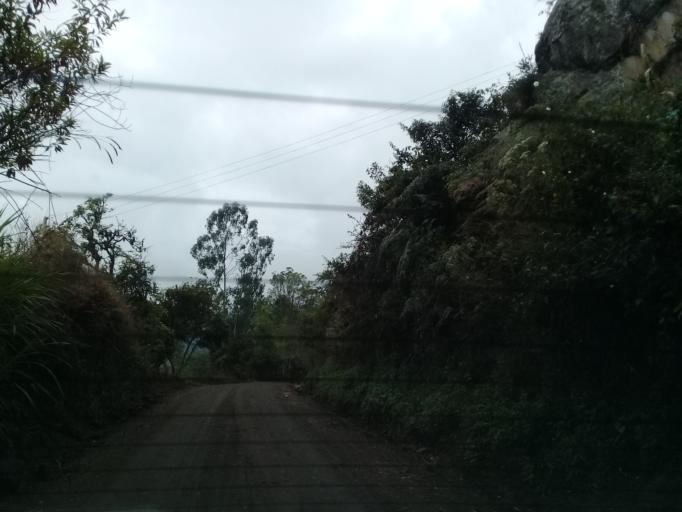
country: CO
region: Cundinamarca
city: Caqueza
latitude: 4.3989
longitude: -73.9848
